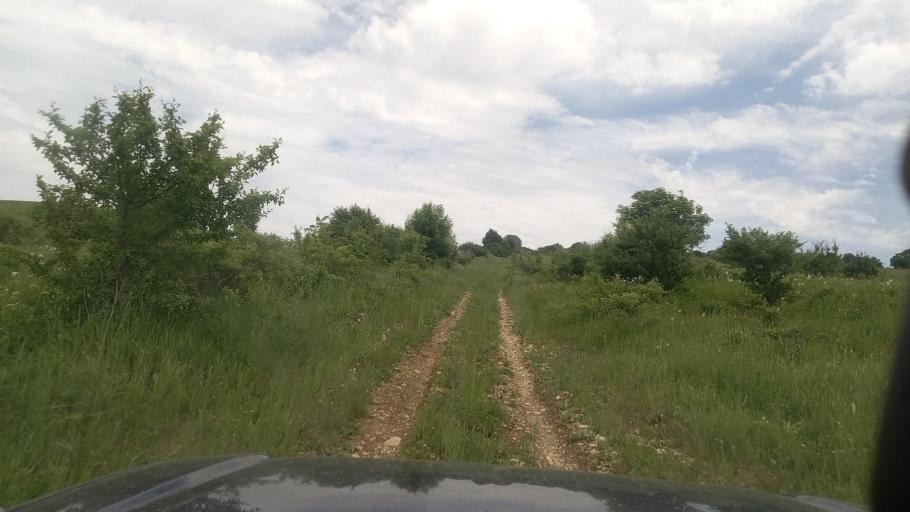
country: RU
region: Karachayevo-Cherkesiya
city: Pregradnaya
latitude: 44.0857
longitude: 41.2120
